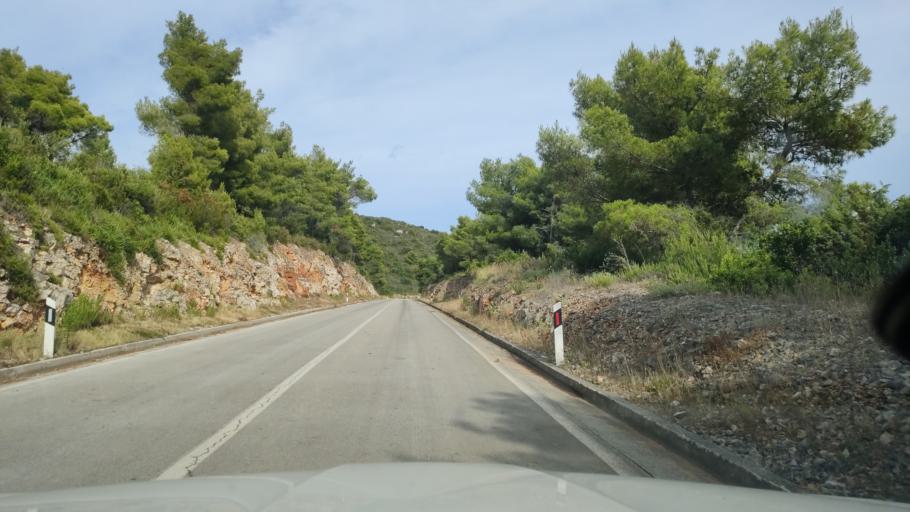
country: HR
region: Splitsko-Dalmatinska
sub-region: Grad Vis
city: Vis
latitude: 43.0318
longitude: 16.2037
